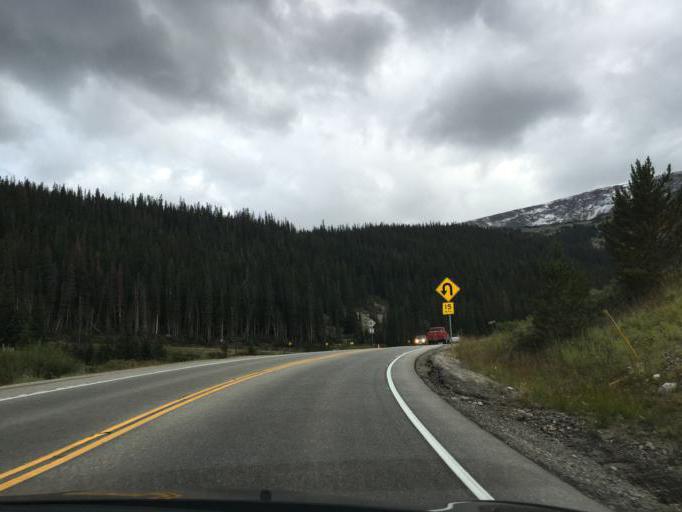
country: US
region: Colorado
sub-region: Summit County
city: Breckenridge
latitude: 39.3817
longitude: -106.0628
